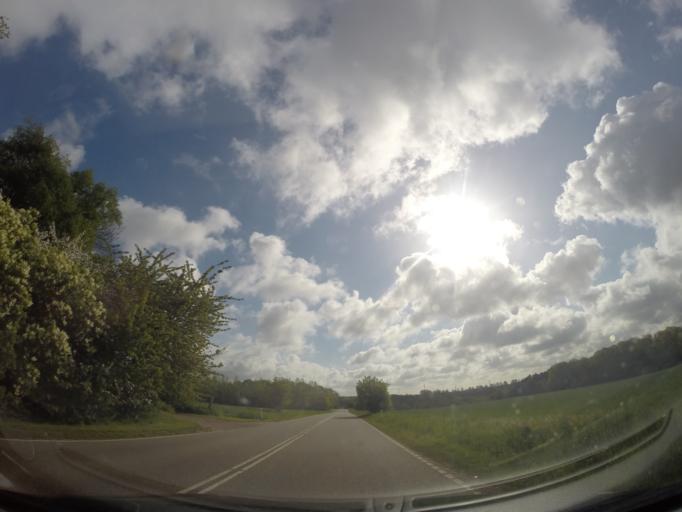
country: DK
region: Capital Region
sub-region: Hoje-Taastrup Kommune
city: Taastrup
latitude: 55.6815
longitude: 12.3072
